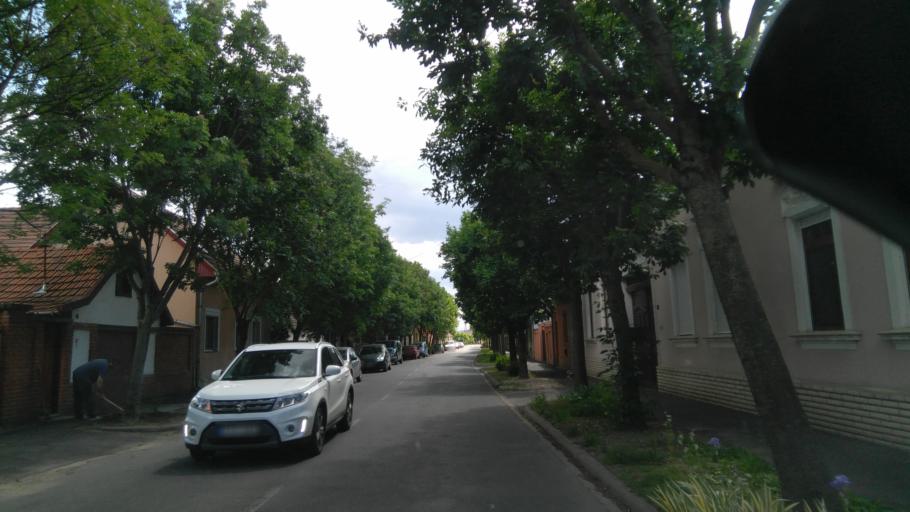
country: HU
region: Bekes
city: Gyula
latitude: 46.6465
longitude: 21.2619
